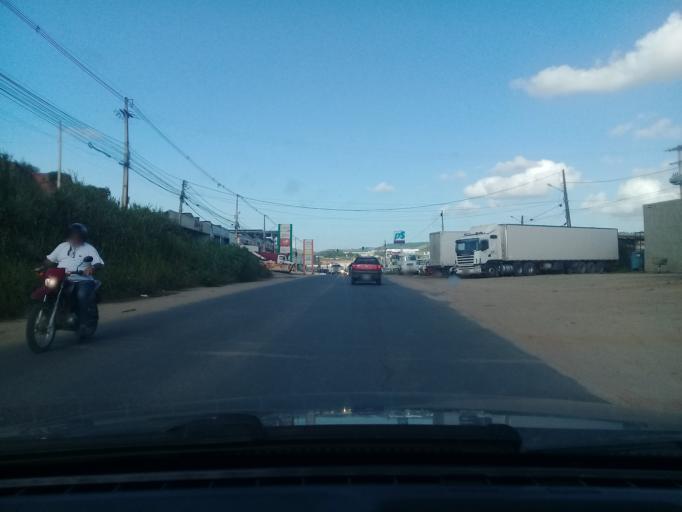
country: BR
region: Pernambuco
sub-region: Vitoria De Santo Antao
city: Vitoria de Santo Antao
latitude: -8.1148
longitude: -35.2773
